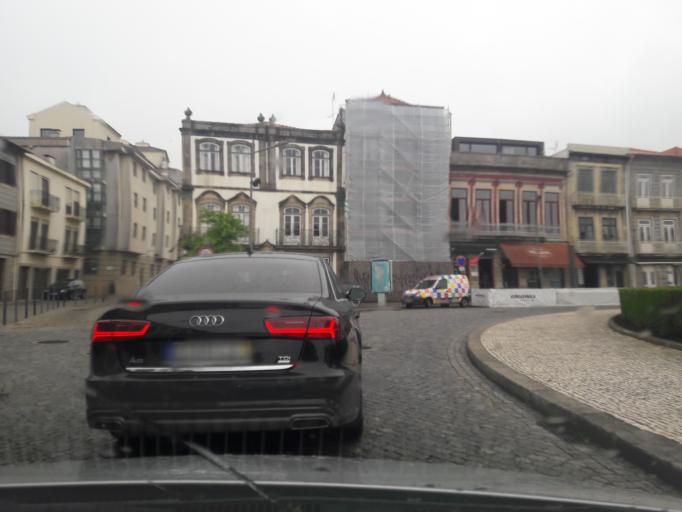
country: PT
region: Porto
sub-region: Vila do Conde
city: Vila do Conde
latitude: 41.3514
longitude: -8.7415
